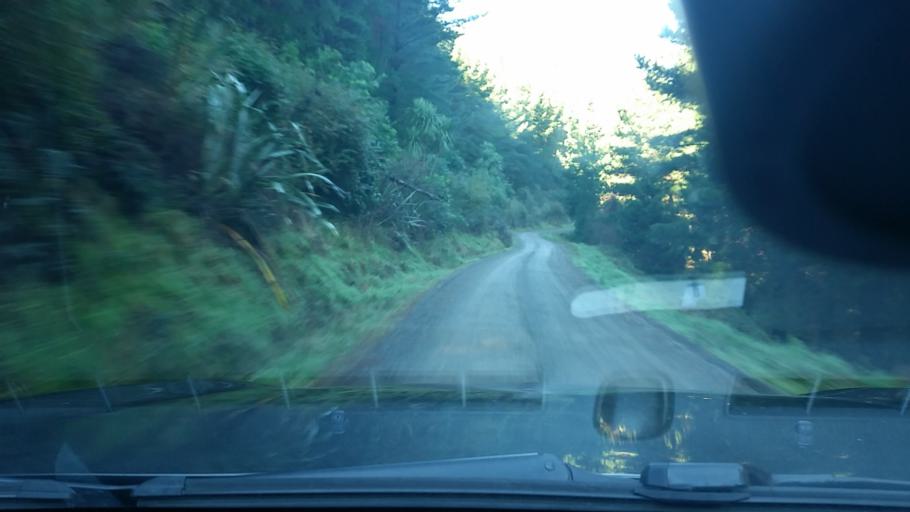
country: NZ
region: Marlborough
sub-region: Marlborough District
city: Blenheim
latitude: -41.6255
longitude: 173.9676
